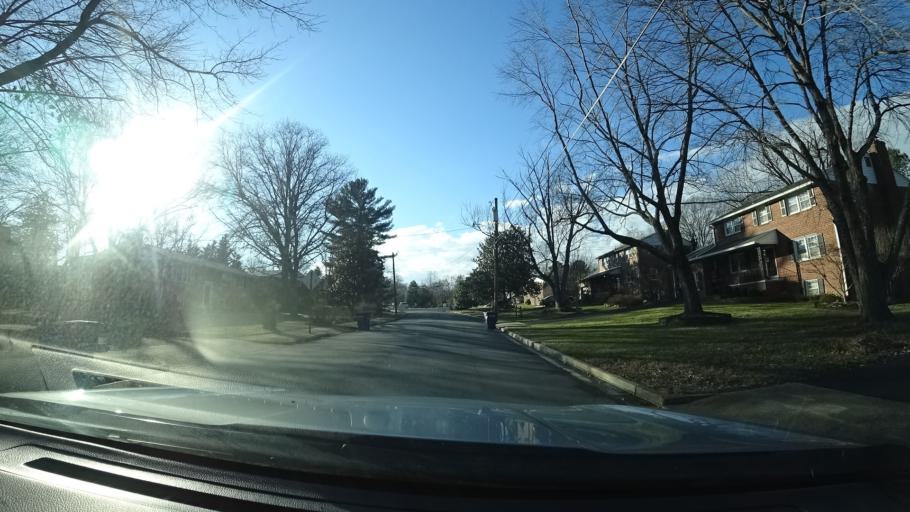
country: US
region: Virginia
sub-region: Fairfax County
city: Herndon
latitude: 38.9749
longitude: -77.3786
